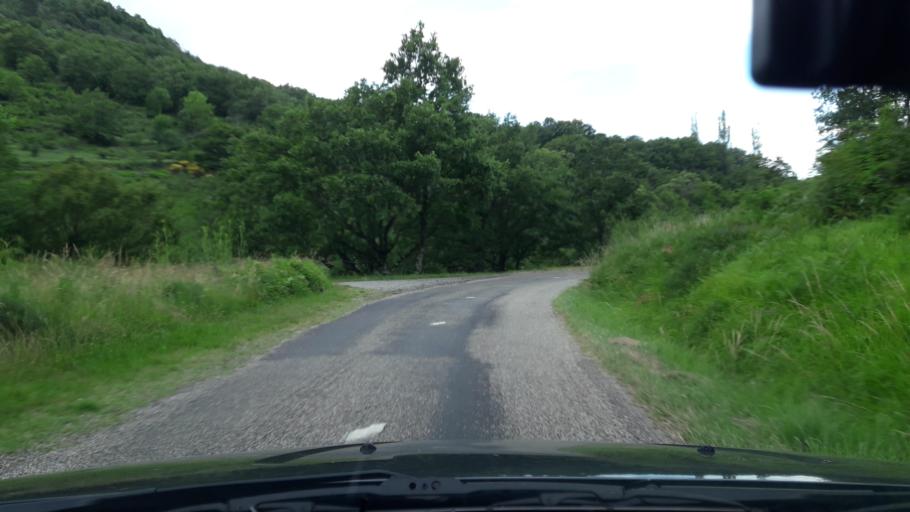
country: FR
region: Rhone-Alpes
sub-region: Departement de l'Ardeche
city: Vesseaux
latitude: 44.6483
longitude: 4.5132
